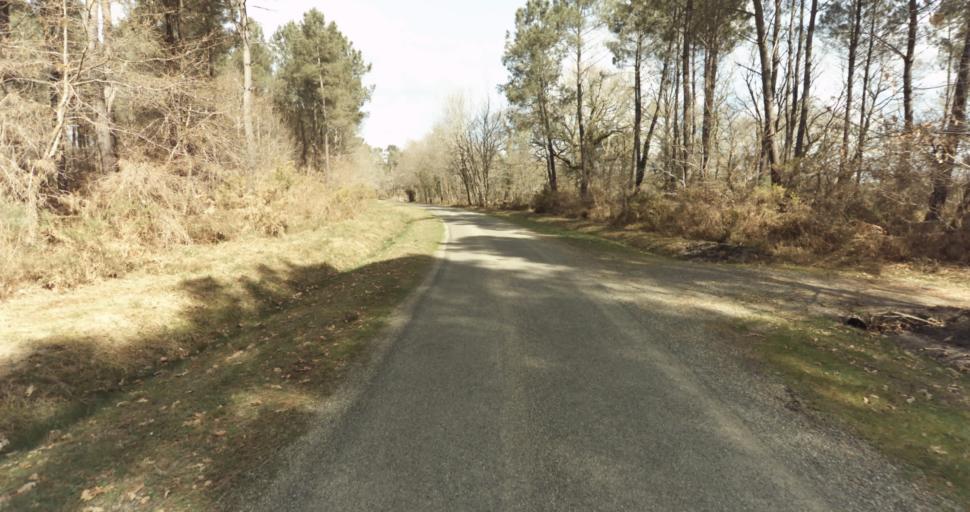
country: FR
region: Aquitaine
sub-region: Departement des Landes
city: Roquefort
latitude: 44.0532
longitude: -0.3369
